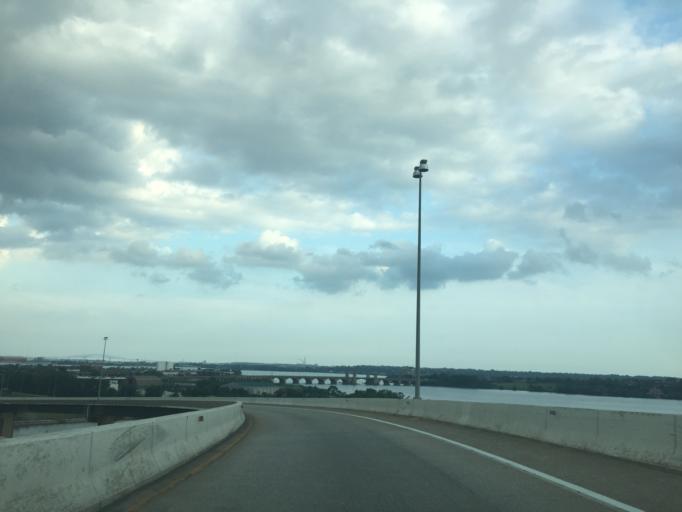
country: US
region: Maryland
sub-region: City of Baltimore
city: Baltimore
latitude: 39.2676
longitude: -76.6241
